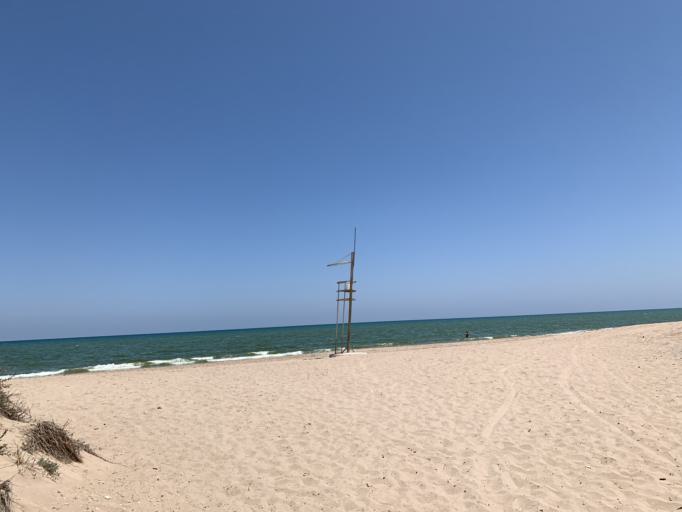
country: ES
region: Valencia
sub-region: Provincia de Valencia
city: Sollana
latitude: 39.3473
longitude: -0.3109
